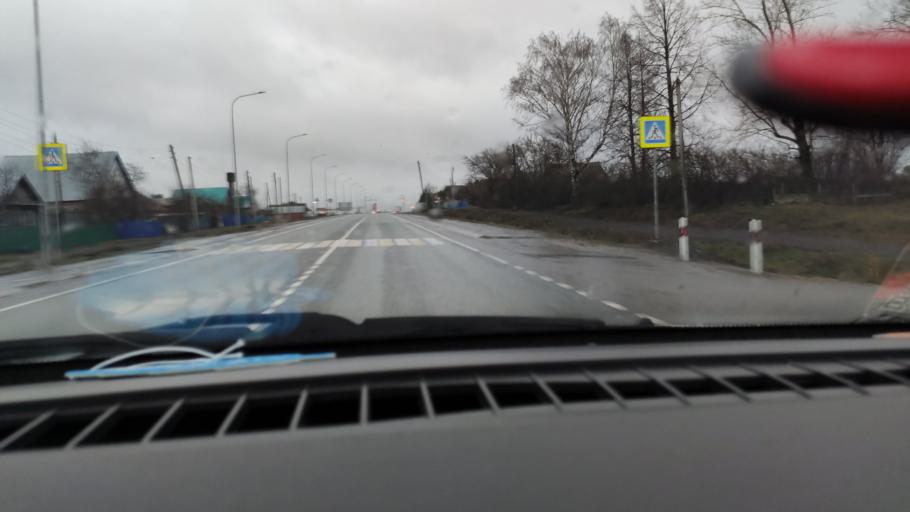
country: RU
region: Tatarstan
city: Mendeleyevsk
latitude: 56.0284
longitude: 52.3719
